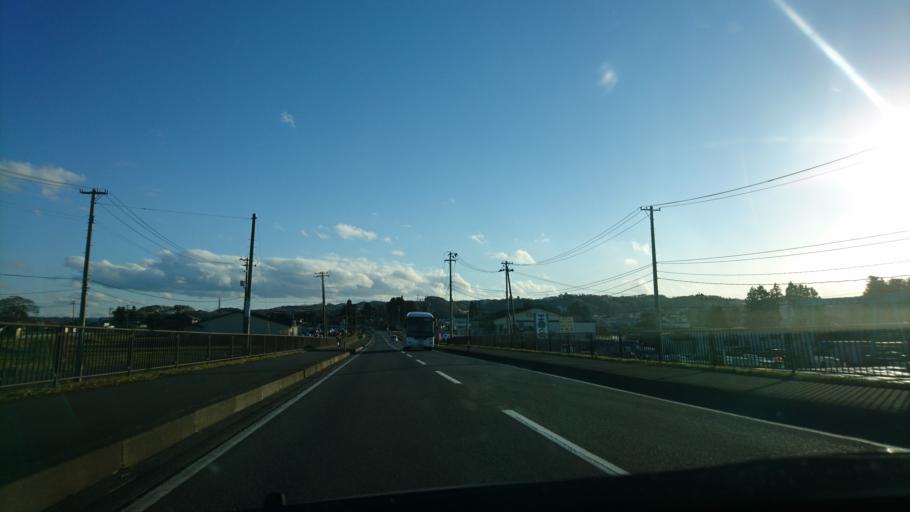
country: JP
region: Iwate
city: Ichinoseki
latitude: 38.9829
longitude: 141.1164
